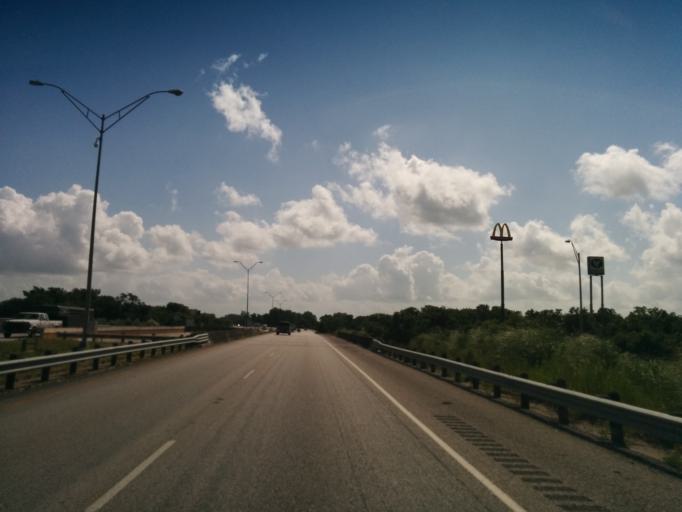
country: US
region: Texas
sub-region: Colorado County
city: Columbus
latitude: 29.6922
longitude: -96.5404
